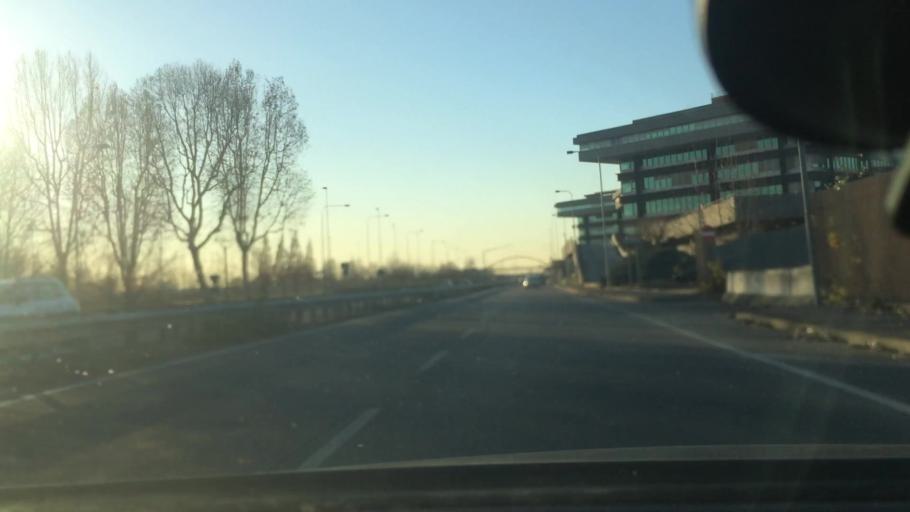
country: IT
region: Lombardy
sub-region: Citta metropolitana di Milano
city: Arese
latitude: 45.5625
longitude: 9.0612
